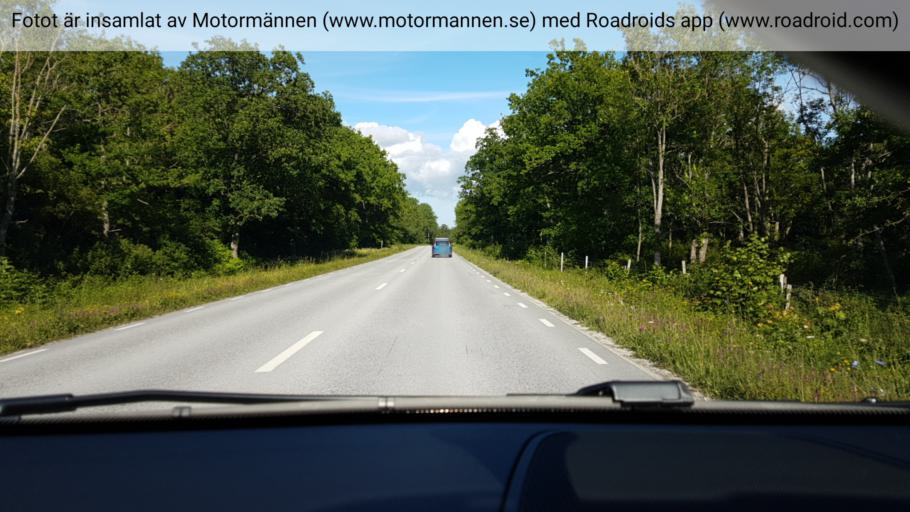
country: SE
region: Gotland
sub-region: Gotland
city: Slite
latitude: 57.7491
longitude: 18.7124
